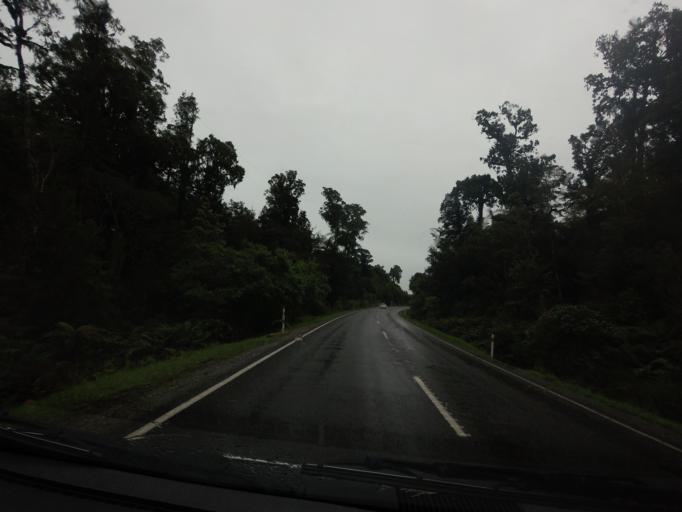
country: NZ
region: Otago
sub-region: Queenstown-Lakes District
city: Wanaka
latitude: -43.8529
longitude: 169.0577
